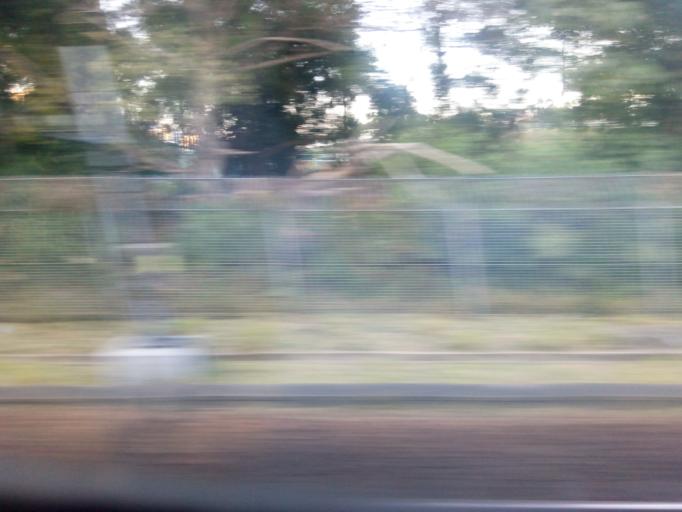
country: HK
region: Tai Po
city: Tai Po
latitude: 22.4441
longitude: 114.1766
